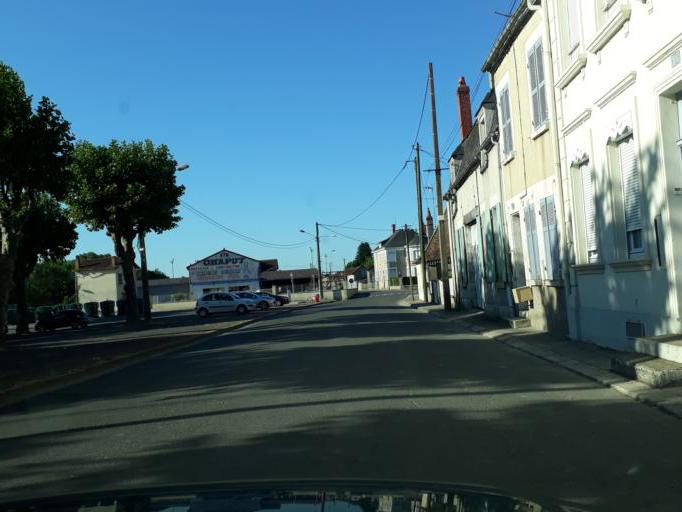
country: FR
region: Bourgogne
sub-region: Departement de la Nievre
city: Cosne-Cours-sur-Loire
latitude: 47.4136
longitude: 2.9223
